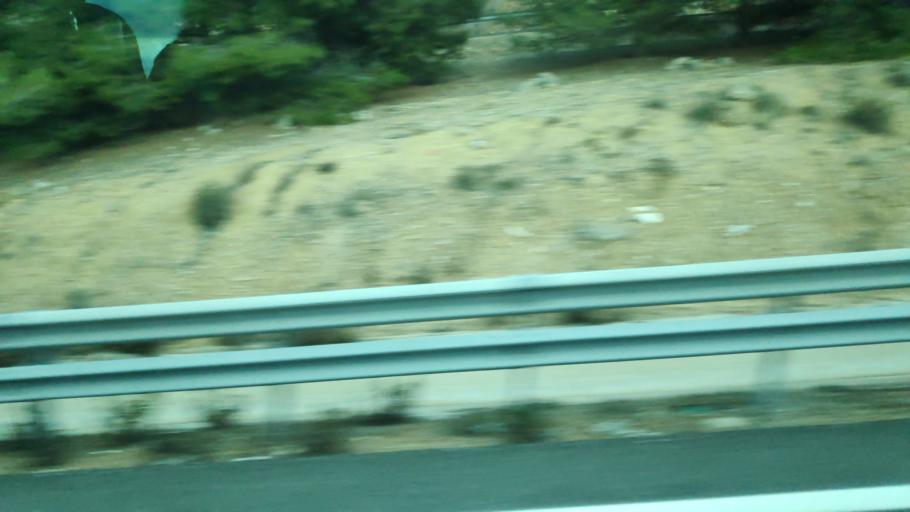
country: ES
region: Castille-La Mancha
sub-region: Provincia de Cuenca
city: Tarancon
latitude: 40.0176
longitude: -3.0332
